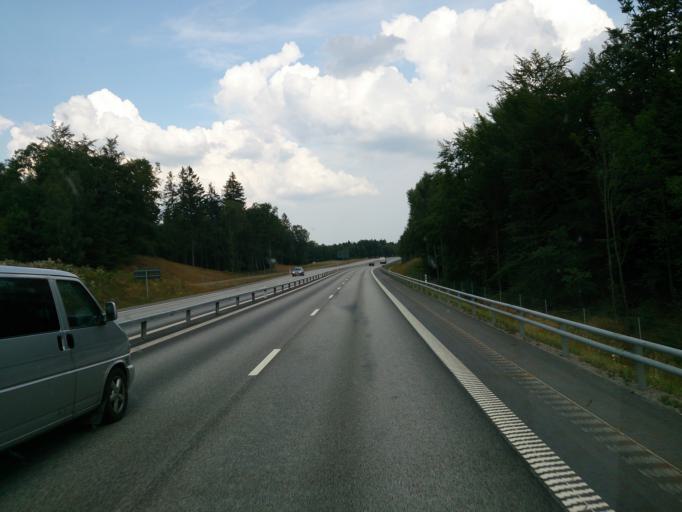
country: SE
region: Skane
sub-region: Horby Kommun
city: Hoerby
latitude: 55.9102
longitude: 13.7552
